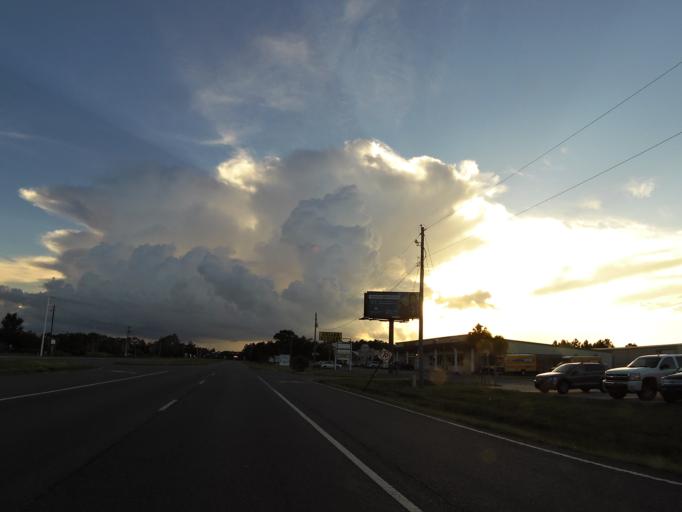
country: US
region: Georgia
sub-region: Camden County
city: St Marys
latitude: 30.7836
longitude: -81.6123
